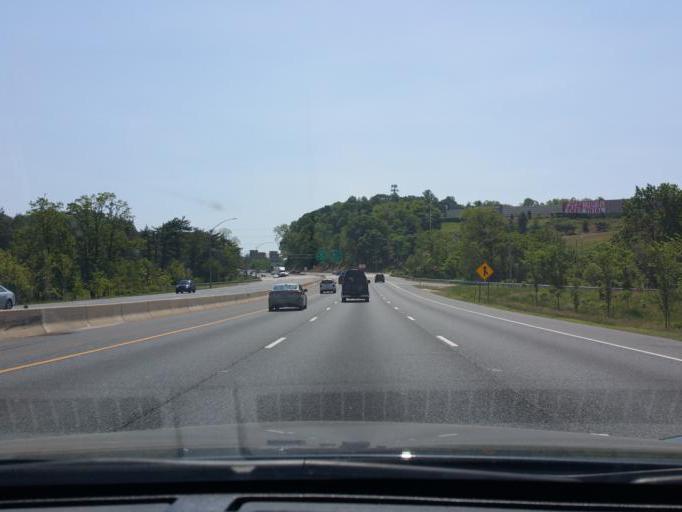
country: US
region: Maryland
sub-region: Baltimore County
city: Hampton
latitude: 39.4036
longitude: -76.5714
